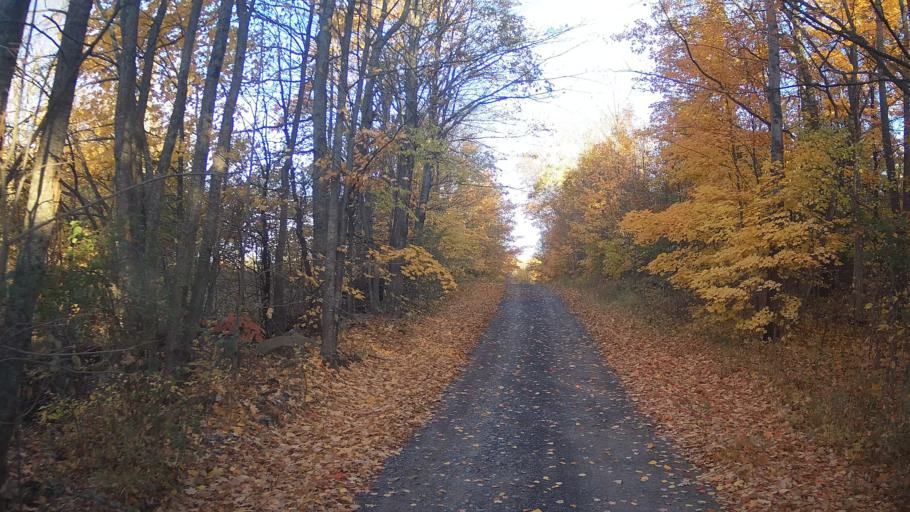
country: CA
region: Ontario
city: Arnprior
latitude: 45.3316
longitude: -76.3685
